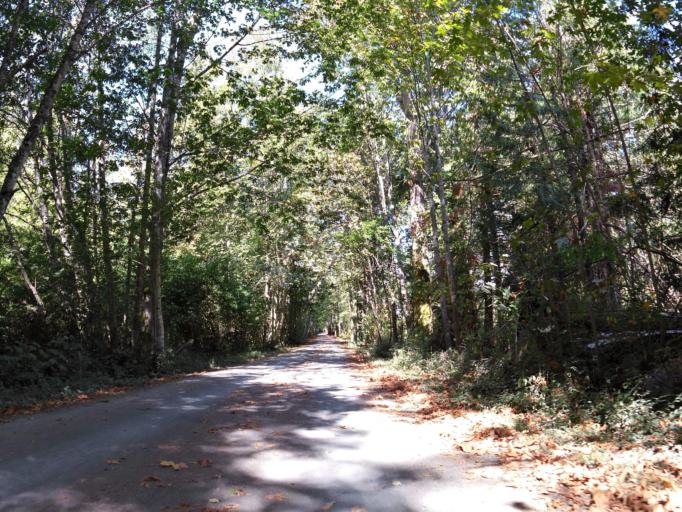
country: CA
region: British Columbia
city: Victoria
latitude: 48.5462
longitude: -123.3850
